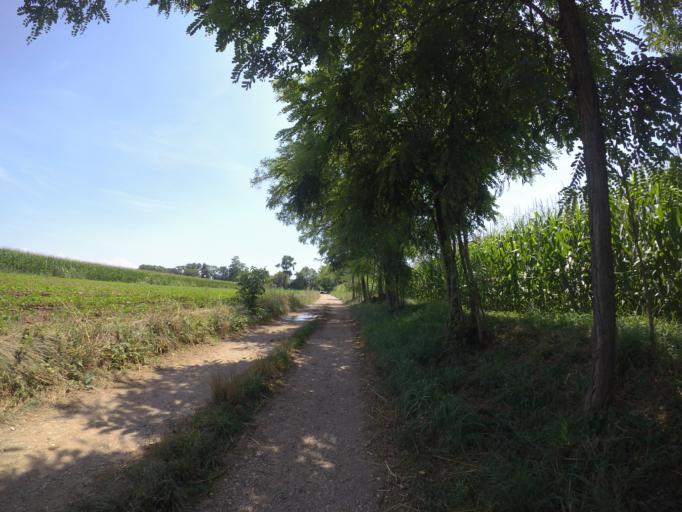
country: IT
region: Friuli Venezia Giulia
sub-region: Provincia di Udine
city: Basiliano
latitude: 45.9780
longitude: 13.0921
